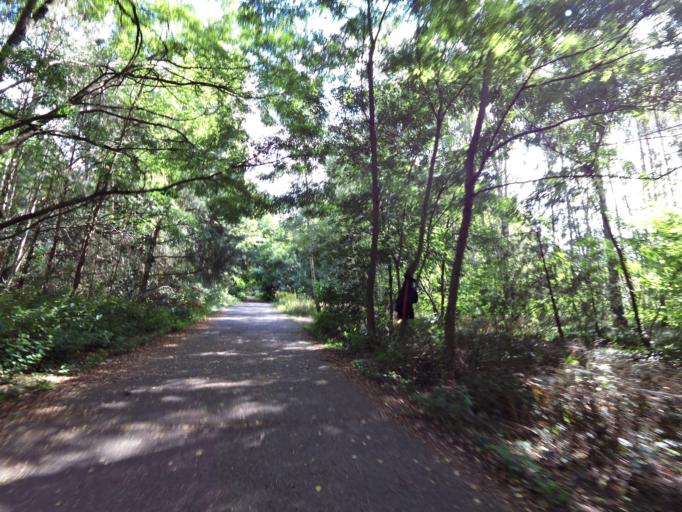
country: DE
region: Berlin
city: Lichtenrade
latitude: 52.3774
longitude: 13.3930
